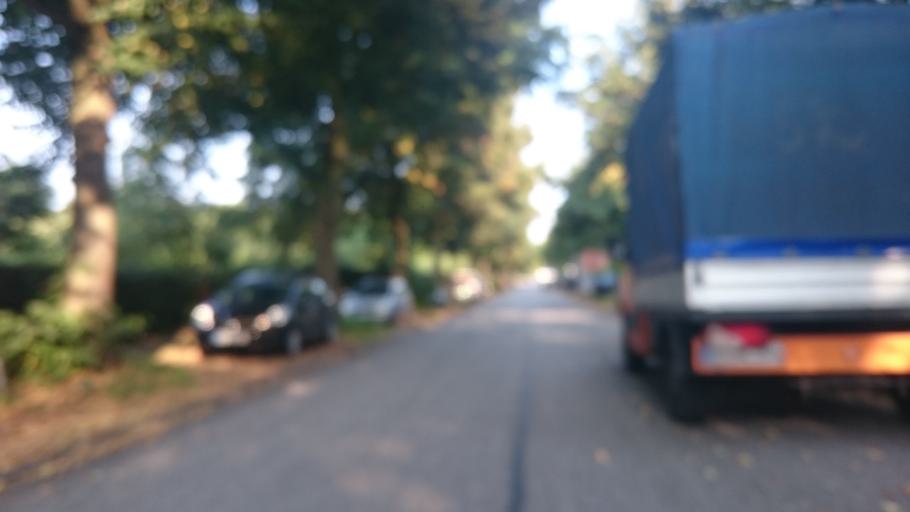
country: DE
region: Hamburg
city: Altona
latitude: 53.5696
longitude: 9.9261
